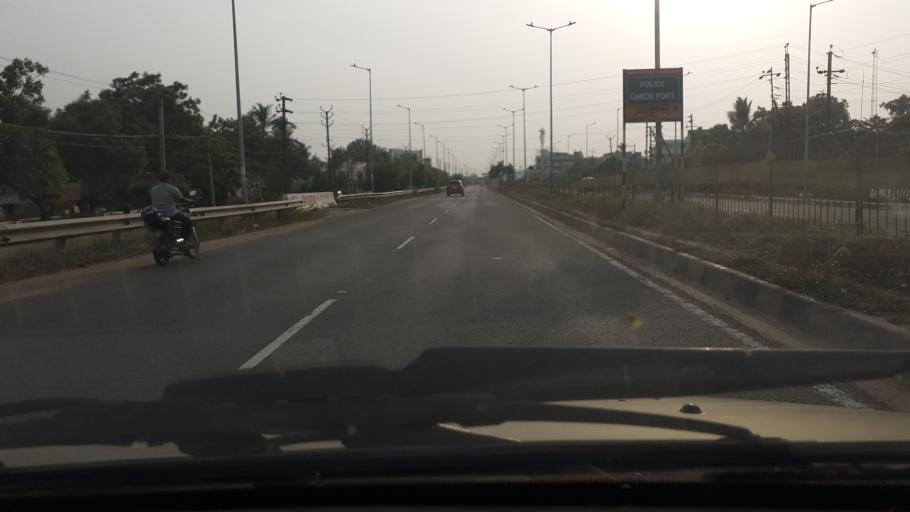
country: IN
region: Tamil Nadu
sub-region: Tirunelveli Kattabo
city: Tirunelveli
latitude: 8.7138
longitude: 77.7772
